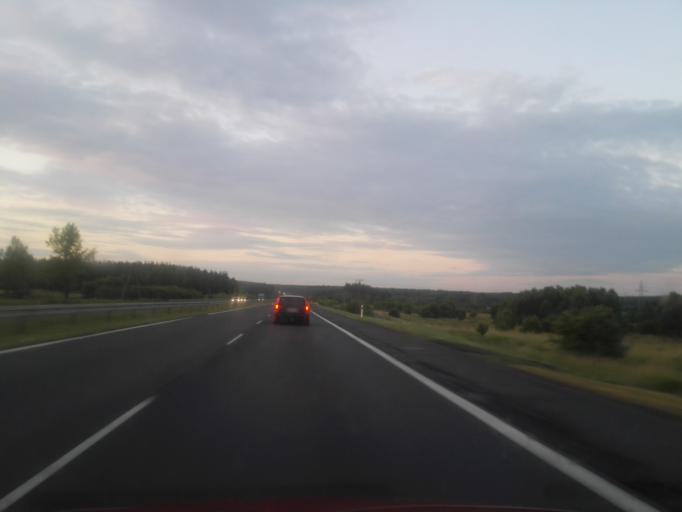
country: PL
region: Lodz Voivodeship
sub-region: Powiat radomszczanski
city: Gomunice
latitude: 51.1495
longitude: 19.4369
